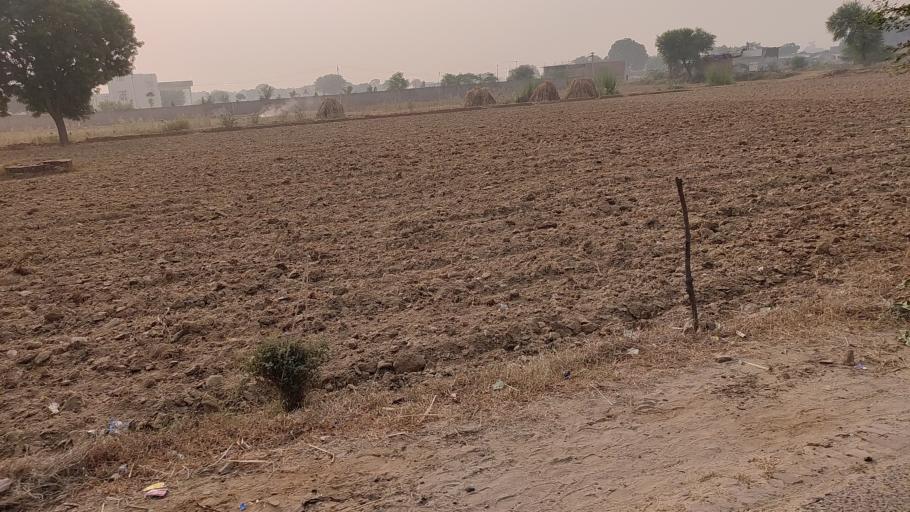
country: IN
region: Uttar Pradesh
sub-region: Mathura
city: Vrindavan
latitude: 27.5569
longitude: 77.7174
